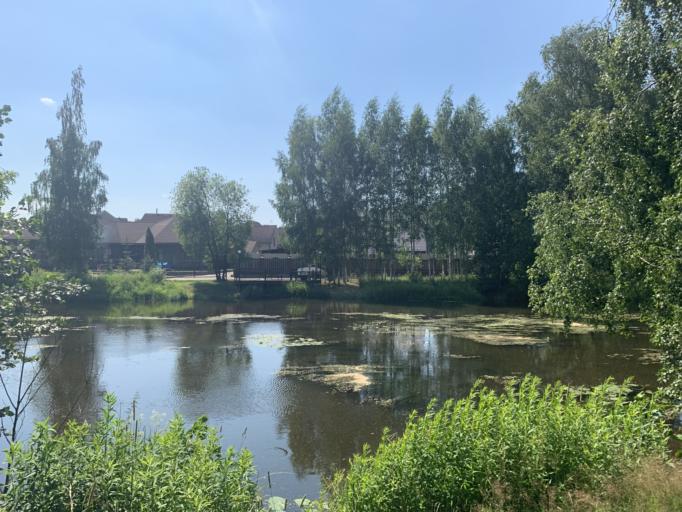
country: RU
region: Moskovskaya
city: Mamontovka
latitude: 55.9692
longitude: 37.8178
